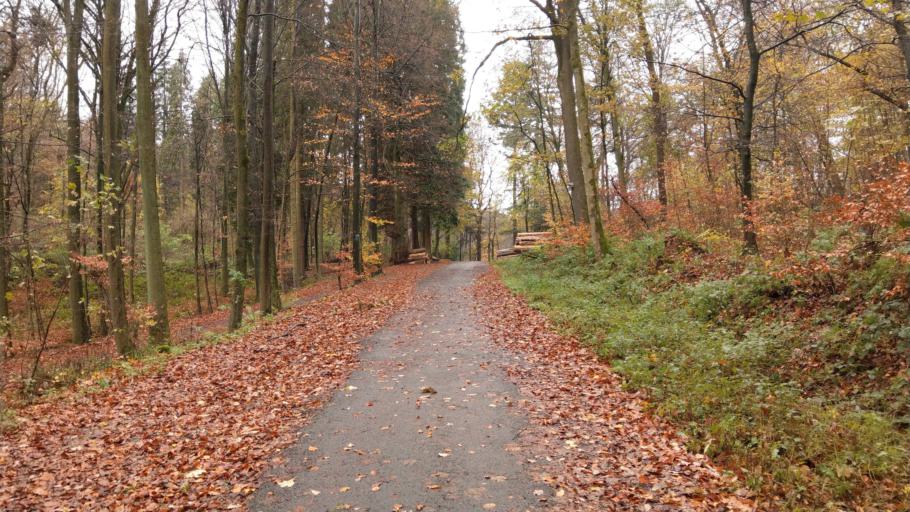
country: DE
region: North Rhine-Westphalia
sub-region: Regierungsbezirk Koln
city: Aachen
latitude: 50.7363
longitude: 6.0706
